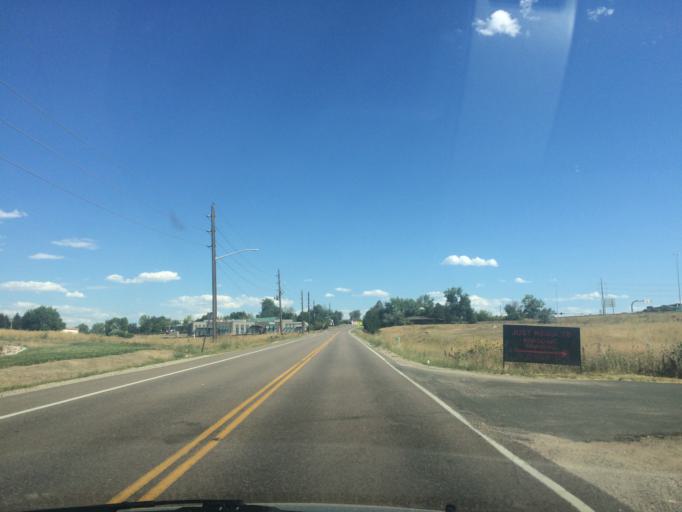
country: US
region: Colorado
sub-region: Broomfield County
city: Broomfield
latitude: 39.9233
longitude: -105.1065
